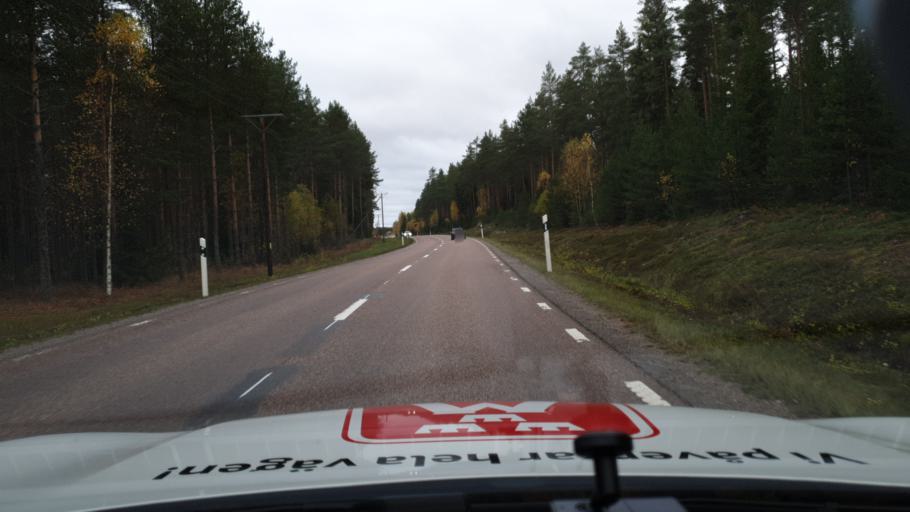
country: SE
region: Gaevleborg
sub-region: Gavle Kommun
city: Hedesunda
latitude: 60.4761
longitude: 16.9406
